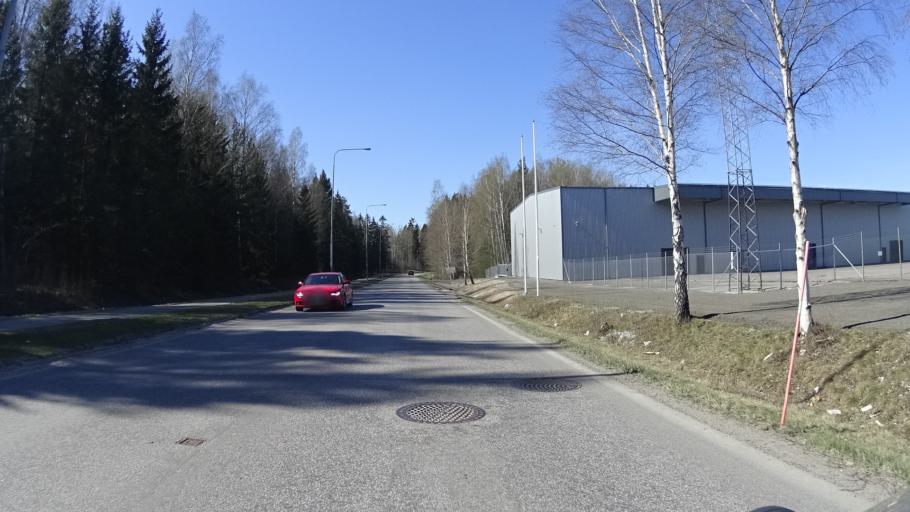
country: SE
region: Soedermanland
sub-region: Katrineholms Kommun
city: Katrineholm
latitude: 58.9923
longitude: 16.2371
